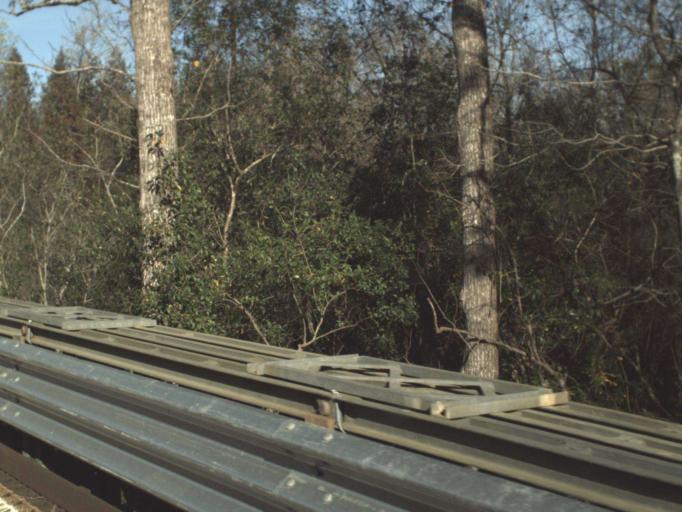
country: US
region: Alabama
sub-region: Escambia County
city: Atmore
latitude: 30.9078
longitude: -87.4798
